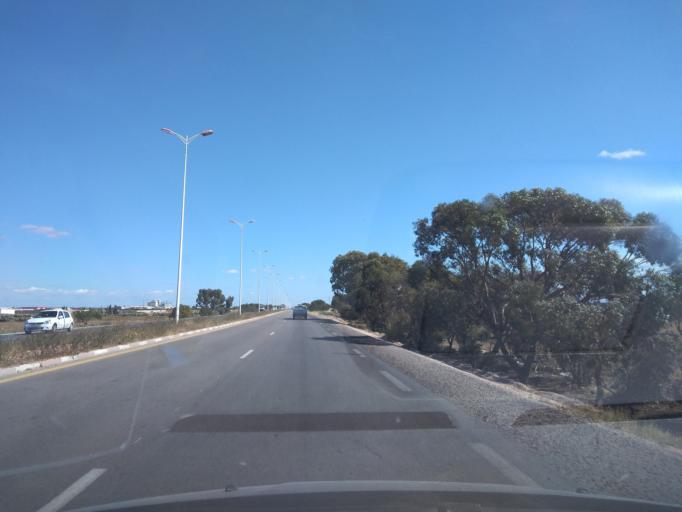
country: TN
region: Safaqis
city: Al Qarmadah
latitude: 34.8477
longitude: 10.7485
